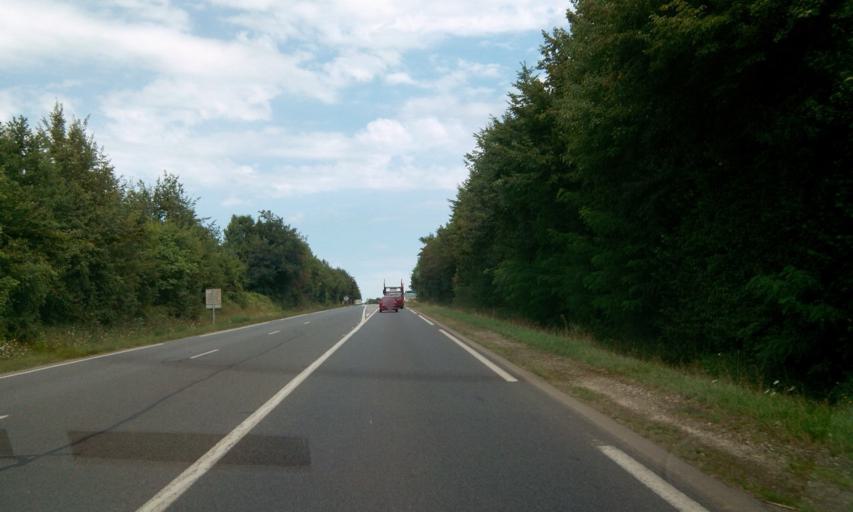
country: FR
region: Poitou-Charentes
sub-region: Departement des Deux-Sevres
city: Melle
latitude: 46.2178
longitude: -0.1568
